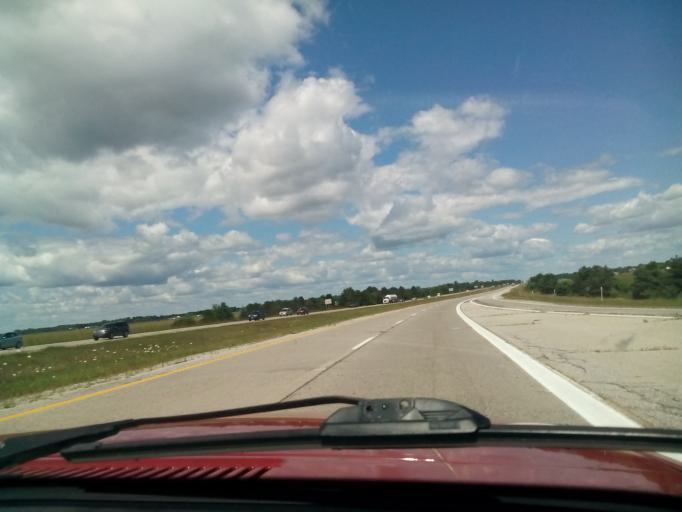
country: US
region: Michigan
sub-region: Bay County
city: Auburn
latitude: 43.6696
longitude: -84.0127
